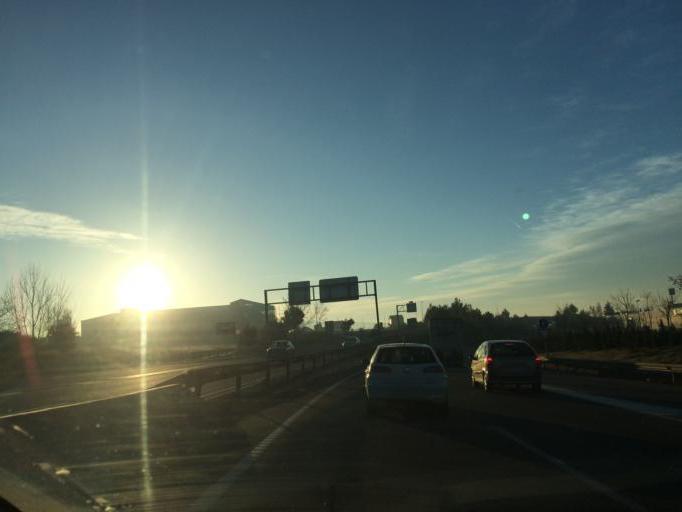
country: ES
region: Catalonia
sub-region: Provincia de Barcelona
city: Sant Fruitos de Bages
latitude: 41.7426
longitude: 1.8474
